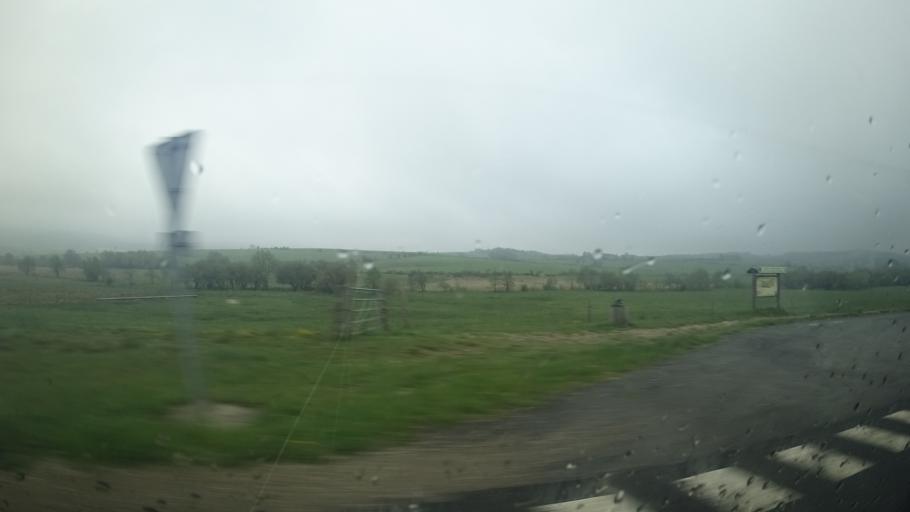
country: FR
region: Midi-Pyrenees
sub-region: Departement de l'Aveyron
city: Severac-le-Chateau
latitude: 44.2467
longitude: 2.9348
